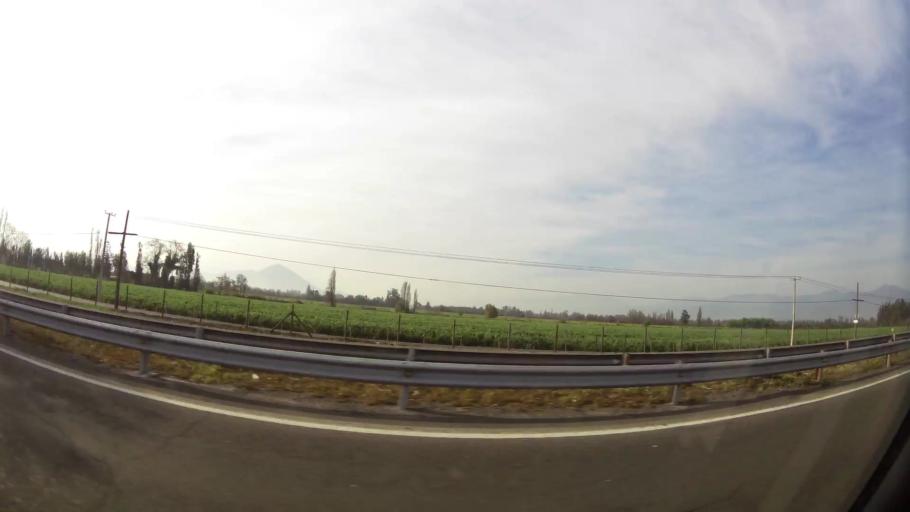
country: CL
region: Santiago Metropolitan
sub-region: Provincia de Talagante
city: Talagante
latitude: -33.6653
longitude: -70.9083
